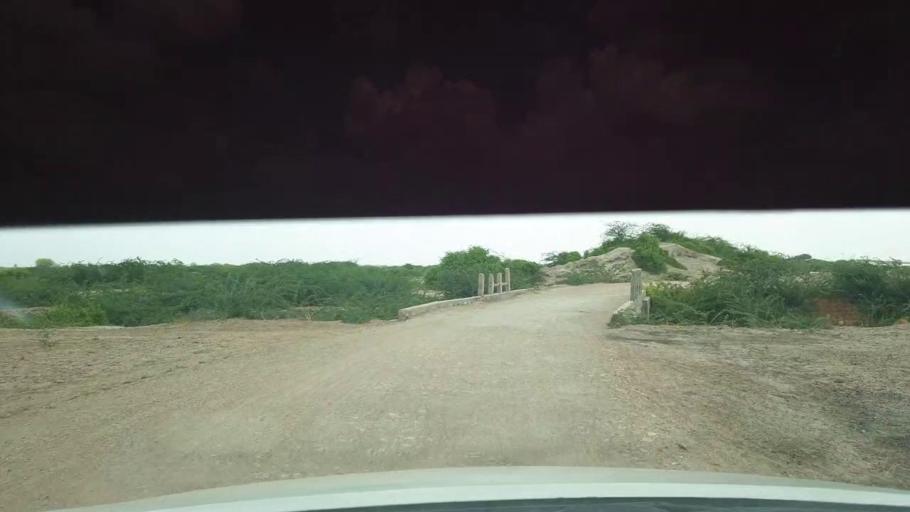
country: PK
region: Sindh
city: Kadhan
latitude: 24.4763
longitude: 69.0638
